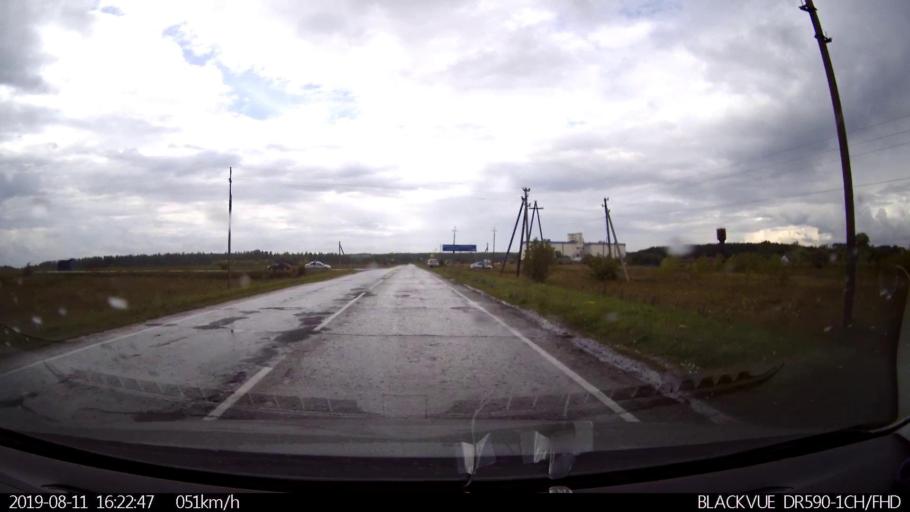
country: RU
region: Ulyanovsk
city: Mayna
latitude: 54.0908
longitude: 47.5912
